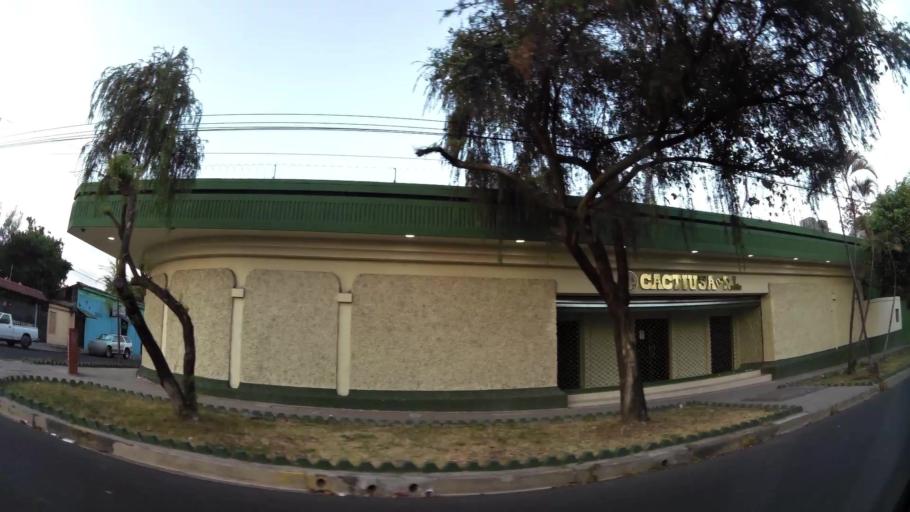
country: SV
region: San Salvador
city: San Salvador
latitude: 13.7097
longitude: -89.1876
